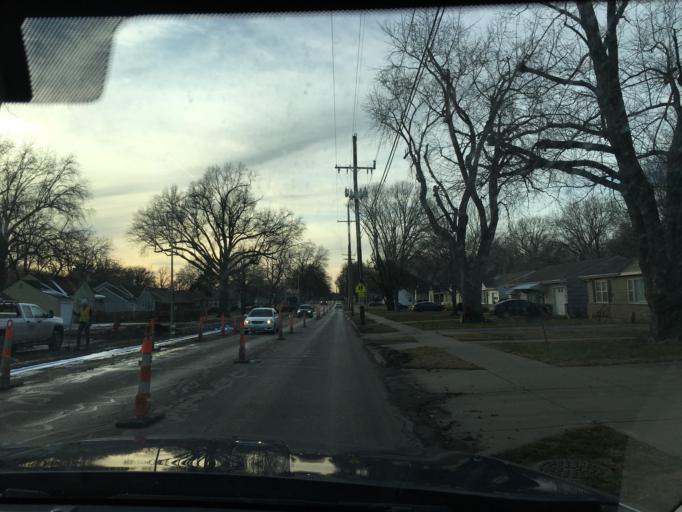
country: US
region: Kansas
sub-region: Johnson County
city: Leawood
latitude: 38.9744
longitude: -94.5983
